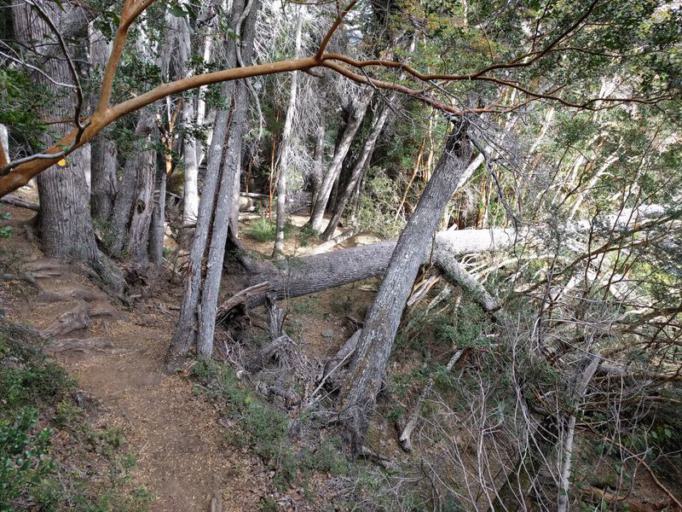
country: AR
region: Chubut
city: Trevelin
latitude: -42.7459
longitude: -71.7464
